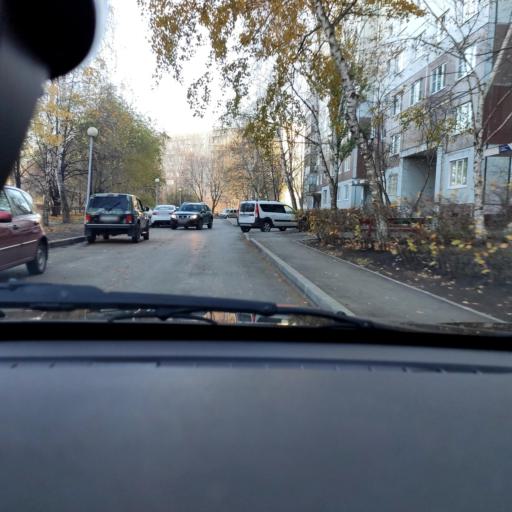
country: RU
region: Samara
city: Tol'yatti
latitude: 53.5397
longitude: 49.3185
